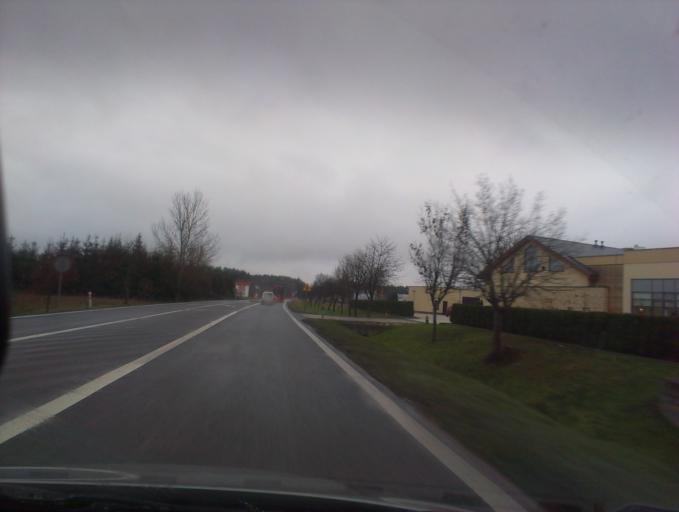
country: PL
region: Greater Poland Voivodeship
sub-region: Powiat chodzieski
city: Budzyn
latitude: 52.9005
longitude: 16.9702
